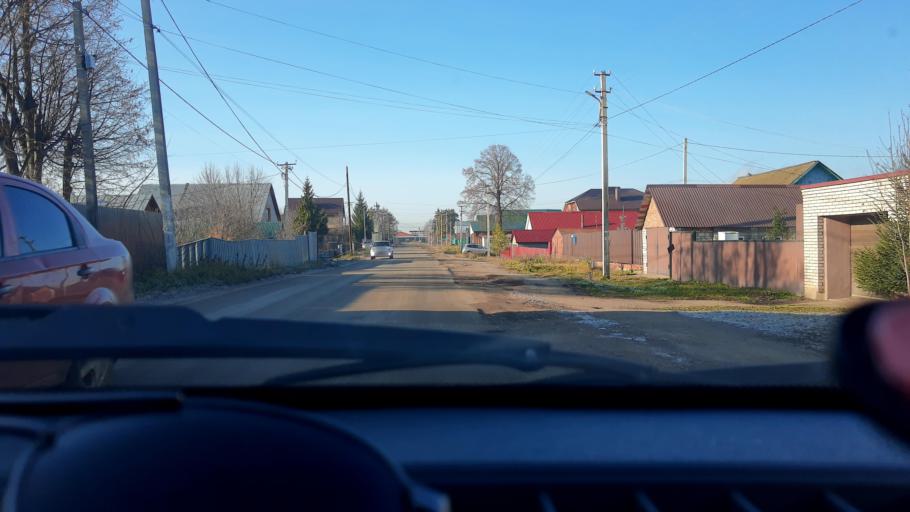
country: RU
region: Bashkortostan
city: Mikhaylovka
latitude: 54.8045
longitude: 55.8856
